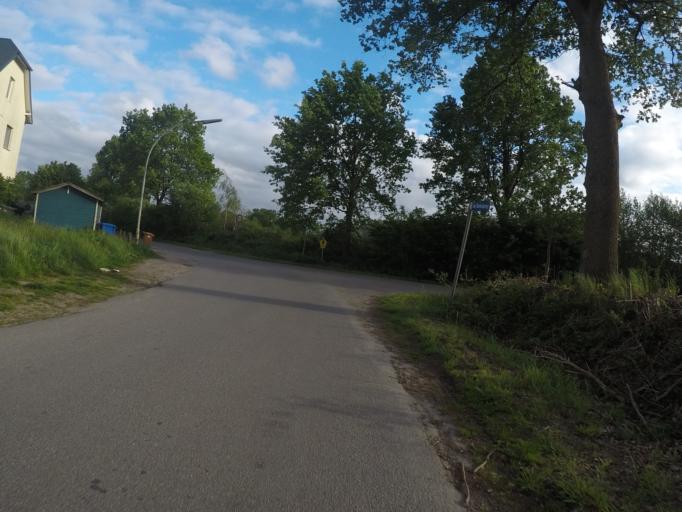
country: DE
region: Schleswig-Holstein
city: Hasloh
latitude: 53.6900
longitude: 9.9225
